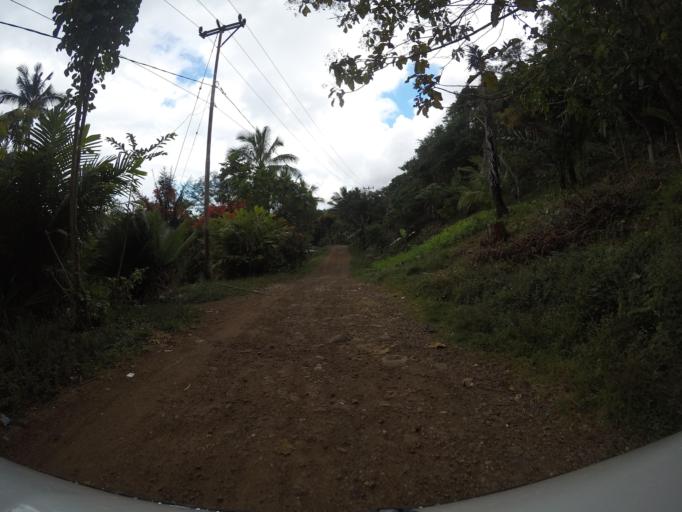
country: TL
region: Baucau
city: Baucau
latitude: -8.6476
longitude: 126.6268
